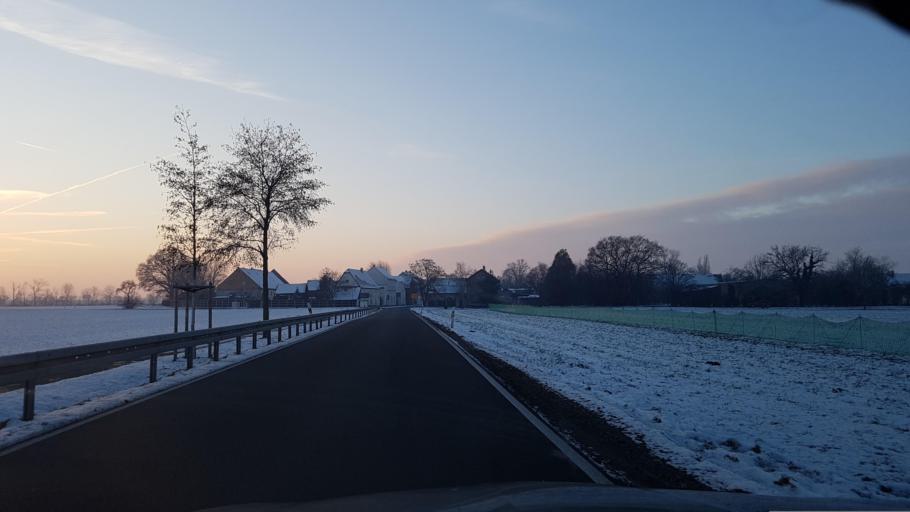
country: DE
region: Saxony
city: Krostitz
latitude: 51.4202
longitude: 12.4567
